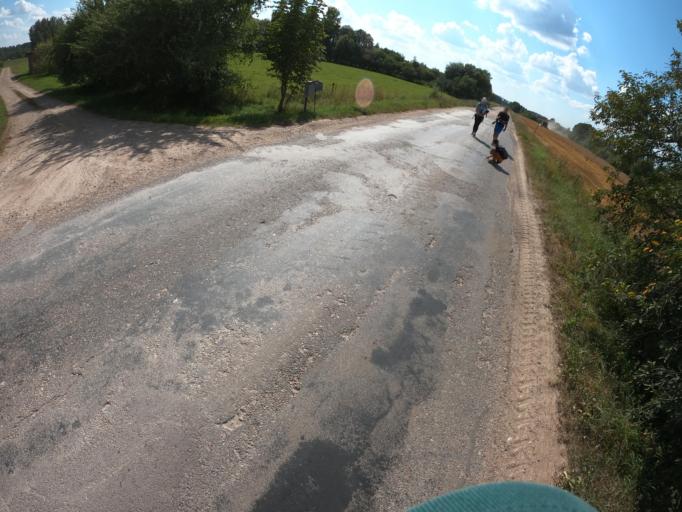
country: LV
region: Priekule
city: Priekule
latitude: 56.3675
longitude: 21.5913
